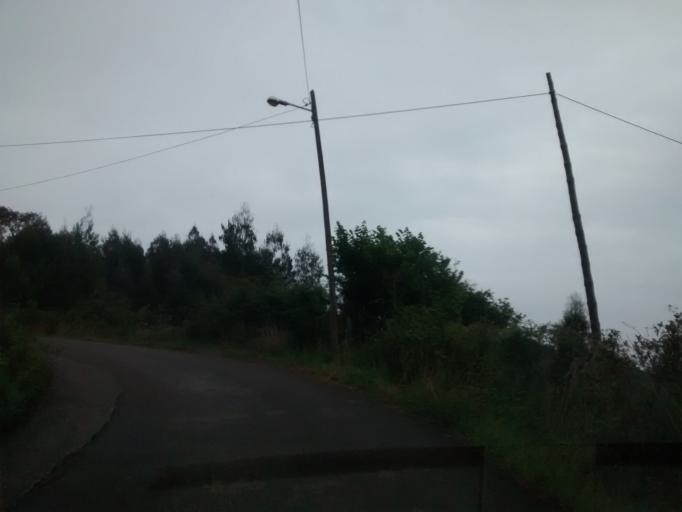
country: ES
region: Asturias
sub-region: Province of Asturias
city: Villaviciosa
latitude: 43.5415
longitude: -5.4079
